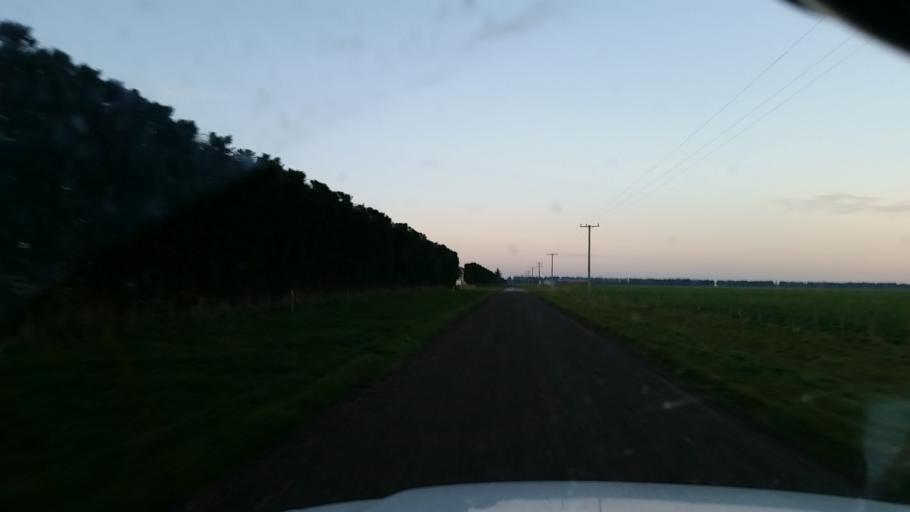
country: NZ
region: Canterbury
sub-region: Ashburton District
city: Tinwald
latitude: -43.9495
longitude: 171.5876
